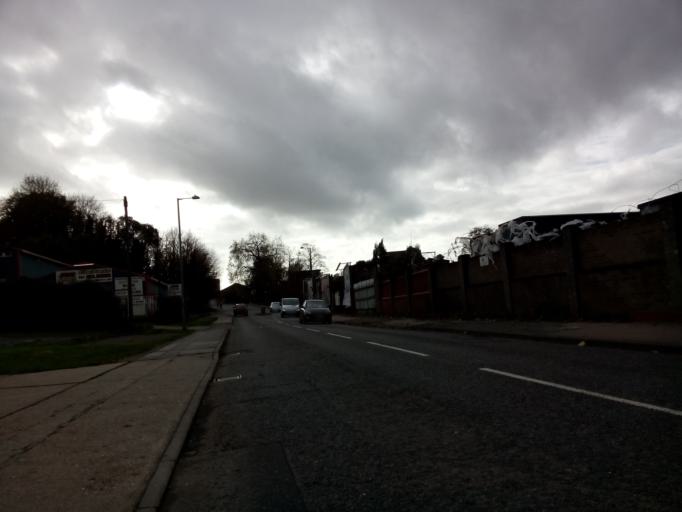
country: GB
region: England
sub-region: Suffolk
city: Ipswich
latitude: 52.0464
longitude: 1.1664
